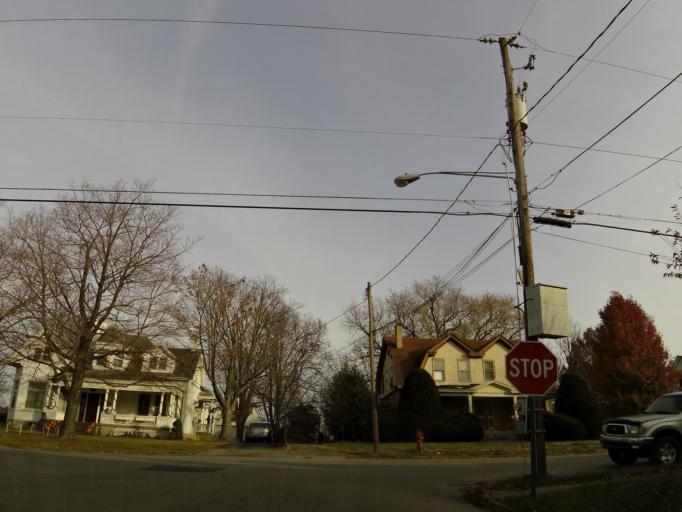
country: US
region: Kentucky
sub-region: Harrison County
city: Cynthiana
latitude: 38.3910
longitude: -84.2863
